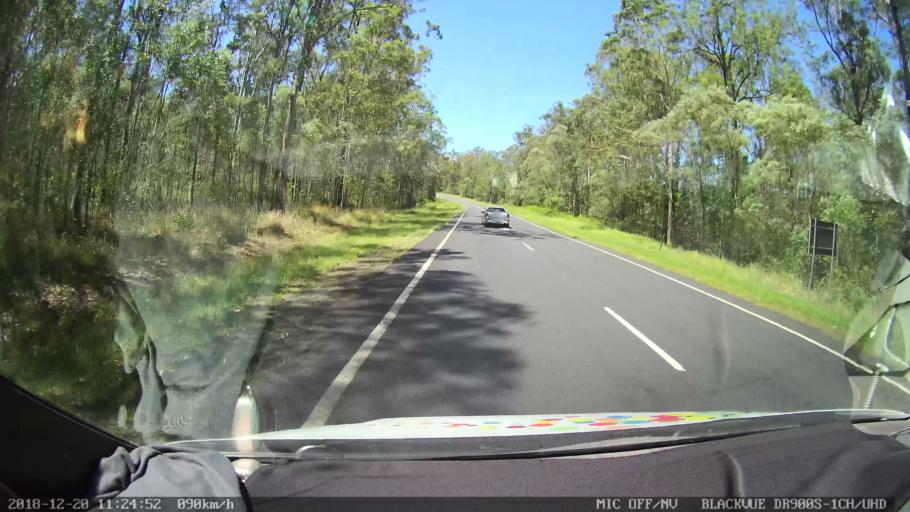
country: AU
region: New South Wales
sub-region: Richmond Valley
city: Casino
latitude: -29.0800
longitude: 153.0007
